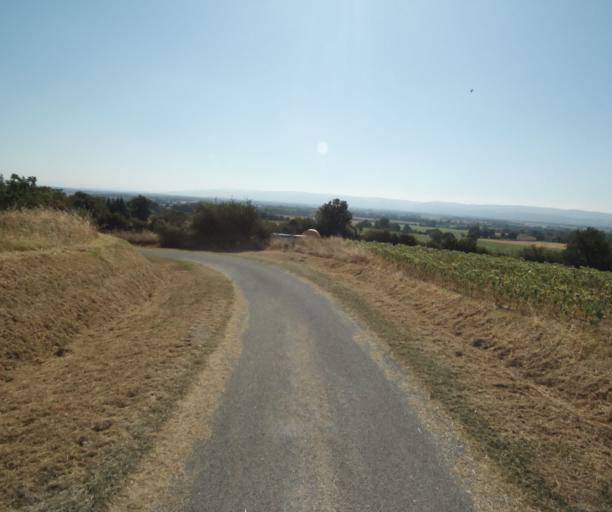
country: FR
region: Midi-Pyrenees
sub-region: Departement de la Haute-Garonne
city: Saint-Felix-Lauragais
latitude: 43.5037
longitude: 1.9396
